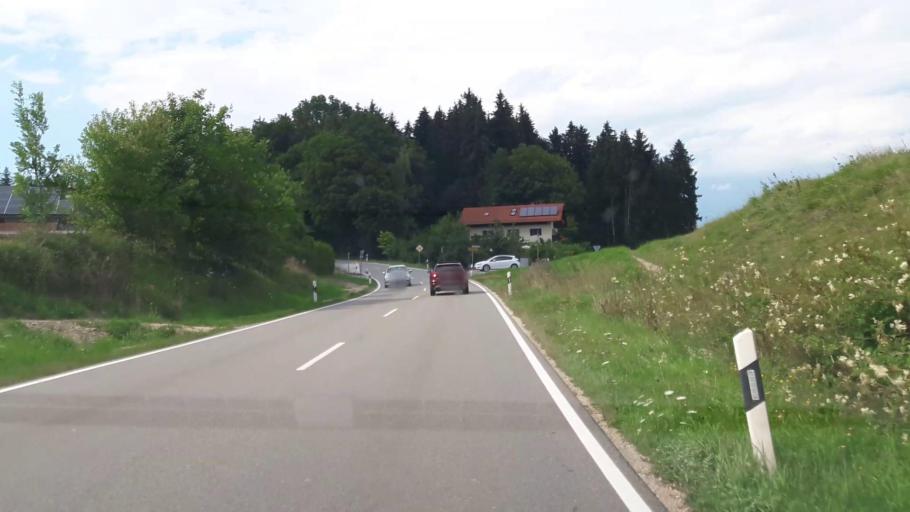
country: DE
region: Bavaria
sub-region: Upper Bavaria
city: Anger
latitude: 47.8068
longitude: 12.8609
